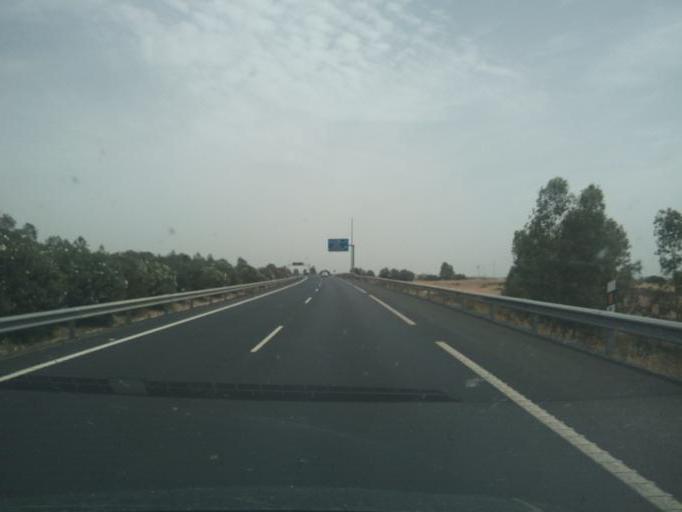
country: ES
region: Andalusia
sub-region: Provincia de Huelva
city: Bollullos par del Condado
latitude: 37.3525
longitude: -6.5797
